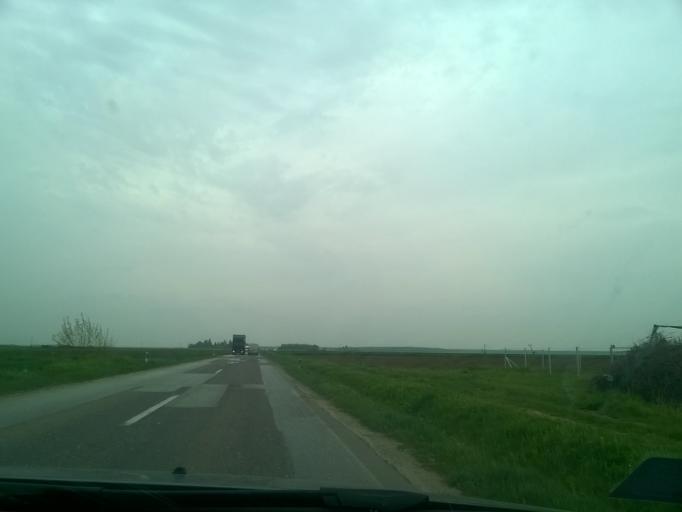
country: RS
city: Hrtkovci
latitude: 44.8656
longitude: 19.7713
